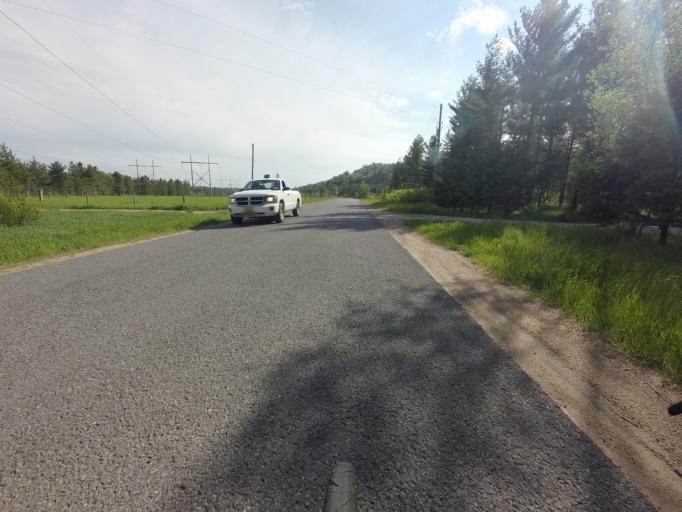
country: US
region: New York
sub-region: St. Lawrence County
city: Gouverneur
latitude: 44.2209
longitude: -75.2380
